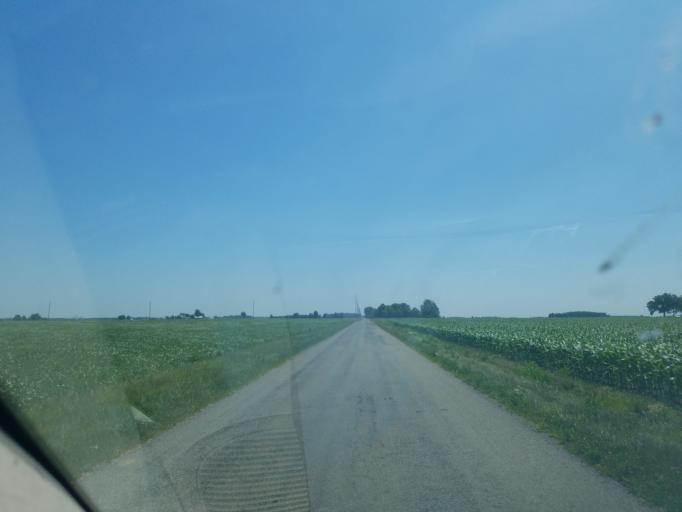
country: US
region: Ohio
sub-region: Mercer County
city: Rockford
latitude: 40.6694
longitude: -84.6949
